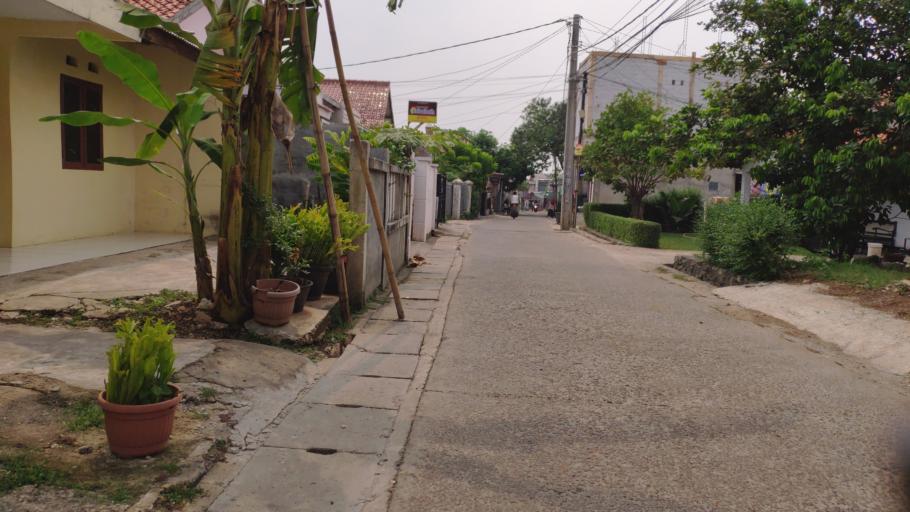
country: ID
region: West Java
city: Depok
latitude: -6.3754
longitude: 106.7998
